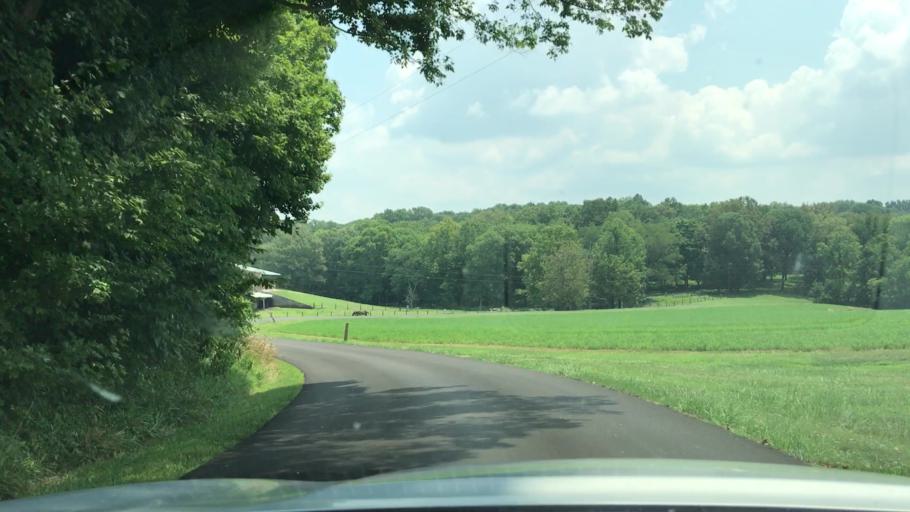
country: US
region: Kentucky
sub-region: Todd County
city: Elkton
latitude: 36.7741
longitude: -87.1432
